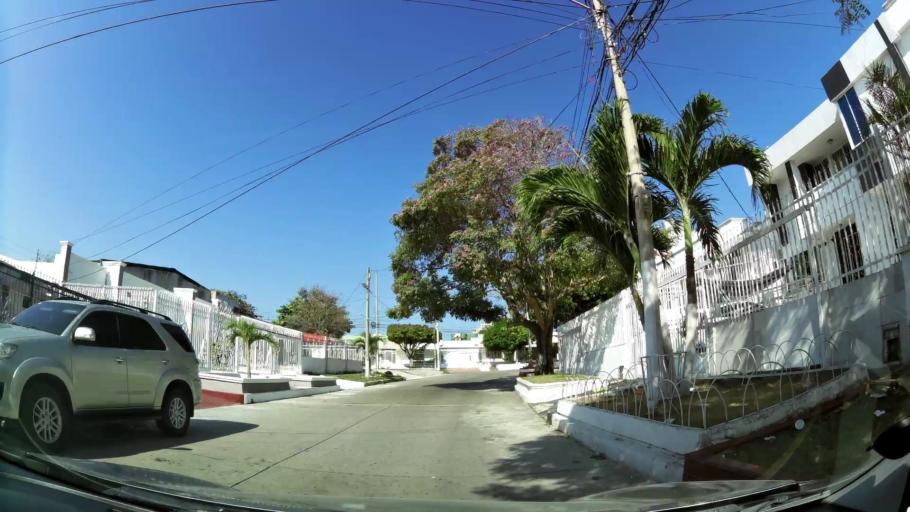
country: CO
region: Atlantico
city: Barranquilla
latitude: 10.9902
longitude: -74.8239
